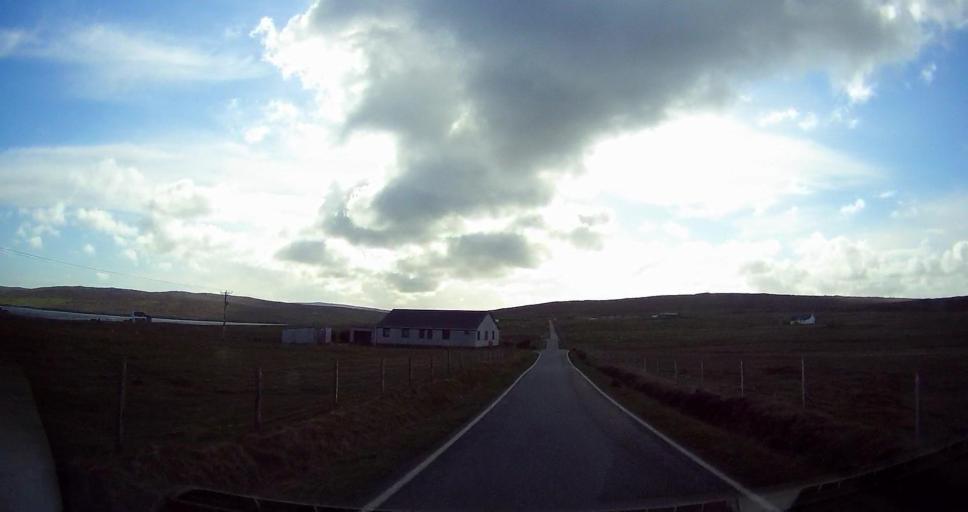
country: GB
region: Scotland
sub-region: Shetland Islands
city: Shetland
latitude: 60.3563
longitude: -1.1505
